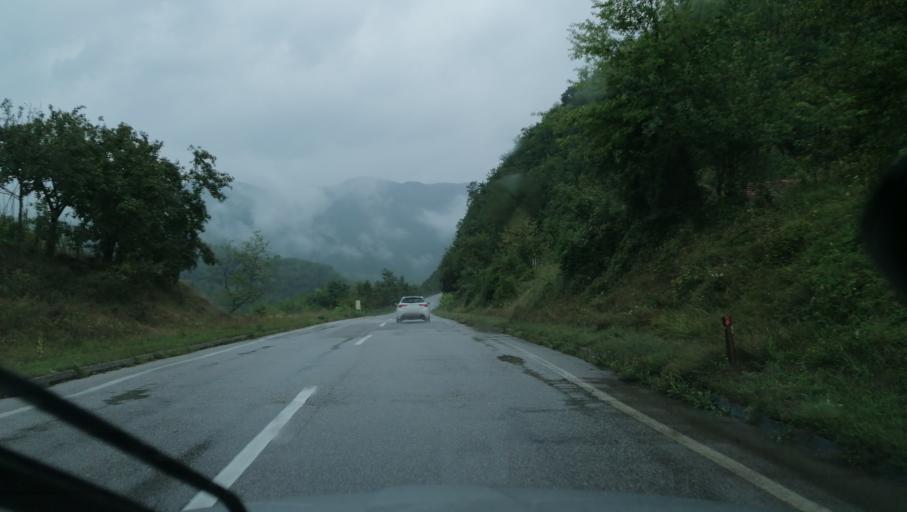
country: BA
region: Republika Srpska
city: Visegrad
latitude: 43.7125
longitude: 19.1689
